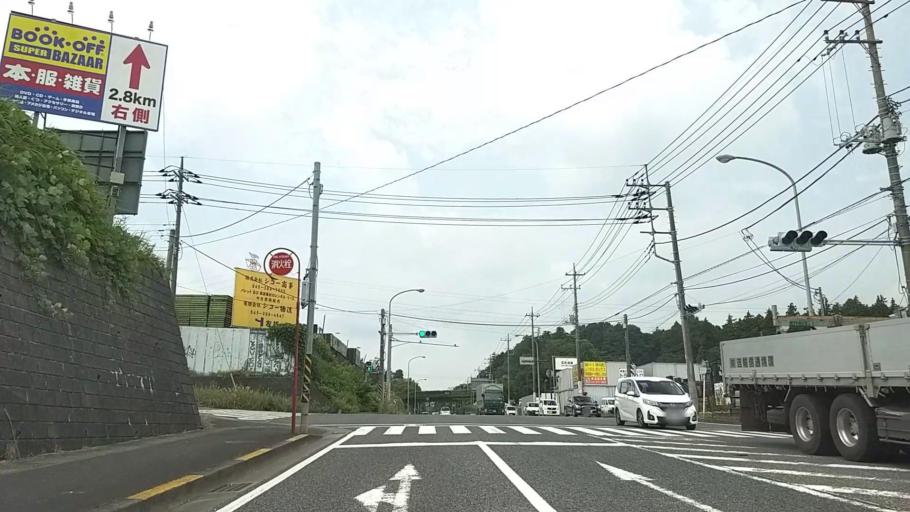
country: JP
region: Kanagawa
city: Minami-rinkan
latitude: 35.4809
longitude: 139.5109
